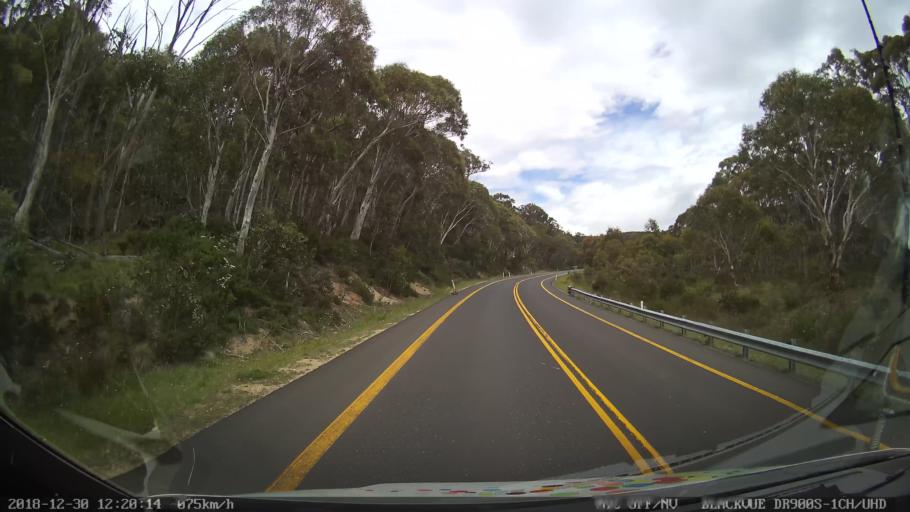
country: AU
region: New South Wales
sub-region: Snowy River
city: Jindabyne
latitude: -36.3469
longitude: 148.5324
